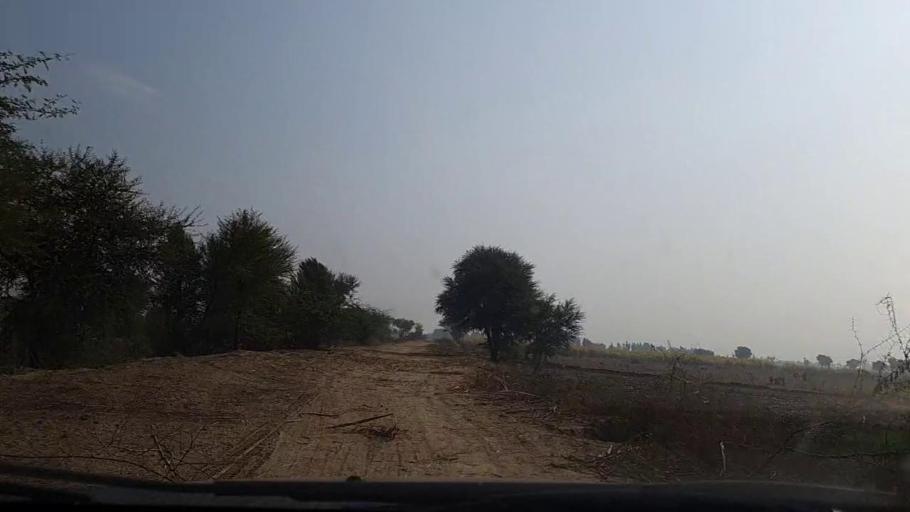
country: PK
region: Sindh
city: Sanghar
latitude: 26.0440
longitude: 68.9911
